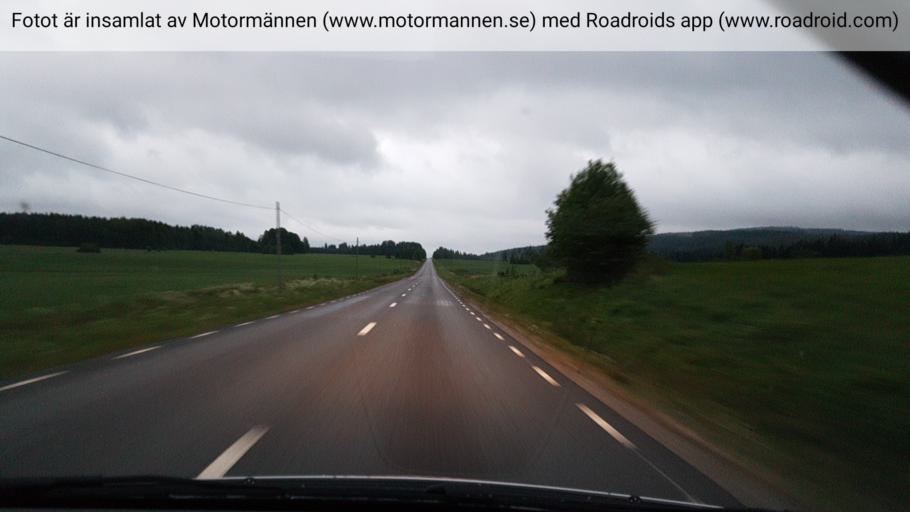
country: SE
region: Vaestmanland
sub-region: Skinnskattebergs Kommun
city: Skinnskatteberg
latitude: 59.9070
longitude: 15.5394
